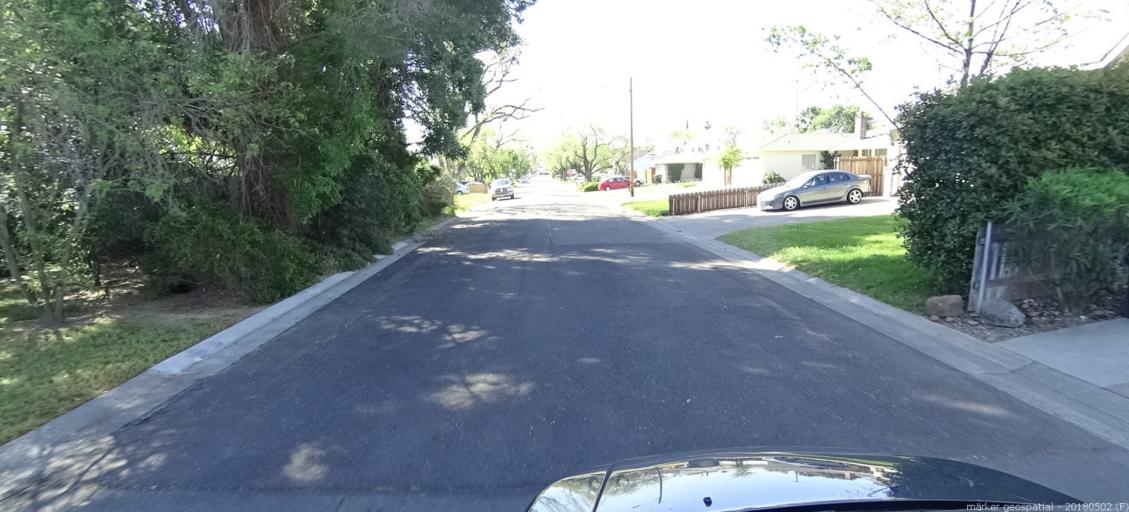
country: US
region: California
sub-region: Sacramento County
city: Arden-Arcade
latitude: 38.6060
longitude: -121.4229
